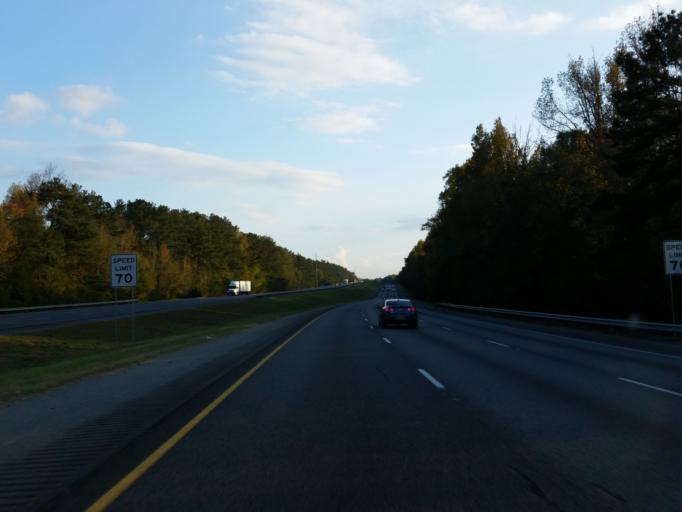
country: US
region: Georgia
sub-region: Bibb County
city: West Point
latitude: 32.7993
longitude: -83.7211
